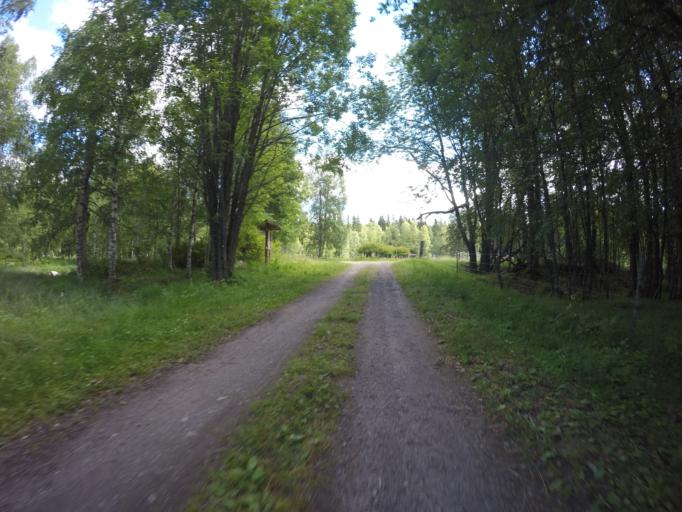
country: SE
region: OErebro
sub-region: Hallefors Kommun
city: Haellefors
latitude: 60.0679
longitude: 14.4621
